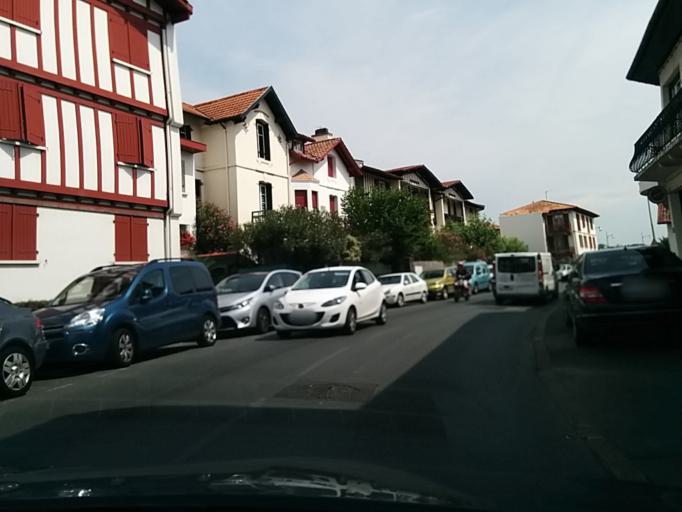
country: FR
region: Aquitaine
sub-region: Departement des Pyrenees-Atlantiques
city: Saint-Jean-de-Luz
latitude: 43.3836
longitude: -1.6675
